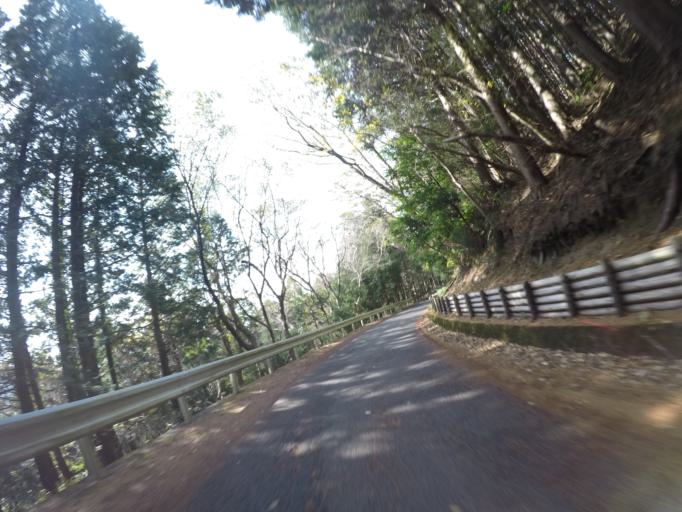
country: JP
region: Shizuoka
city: Heda
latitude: 34.8350
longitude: 138.8476
